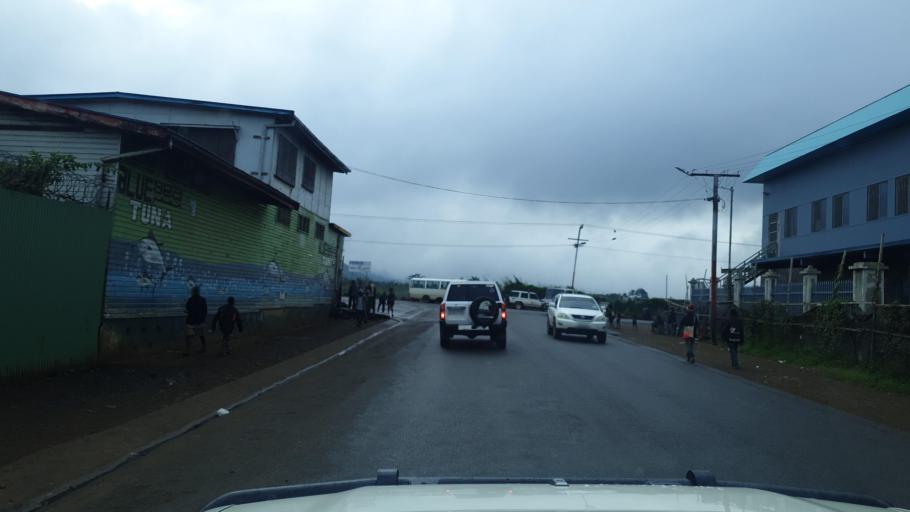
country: PG
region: Eastern Highlands
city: Goroka
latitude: -6.0828
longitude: 145.3892
